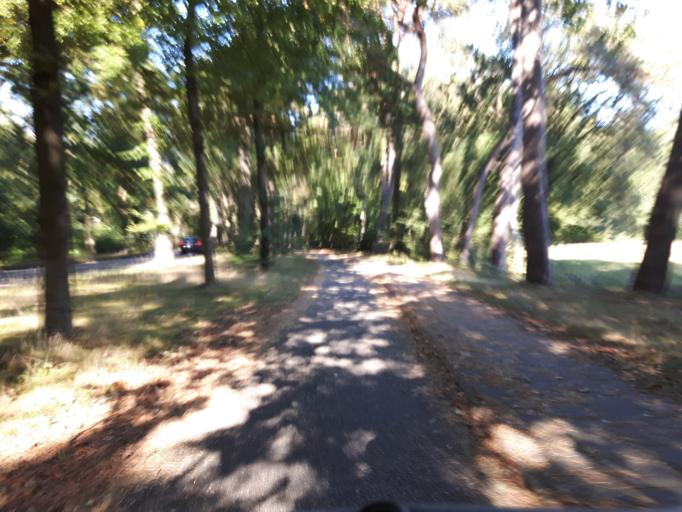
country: NL
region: Utrecht
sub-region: Gemeente Utrechtse Heuvelrug
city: Driebergen-Rijsenburg
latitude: 52.0619
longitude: 5.2835
